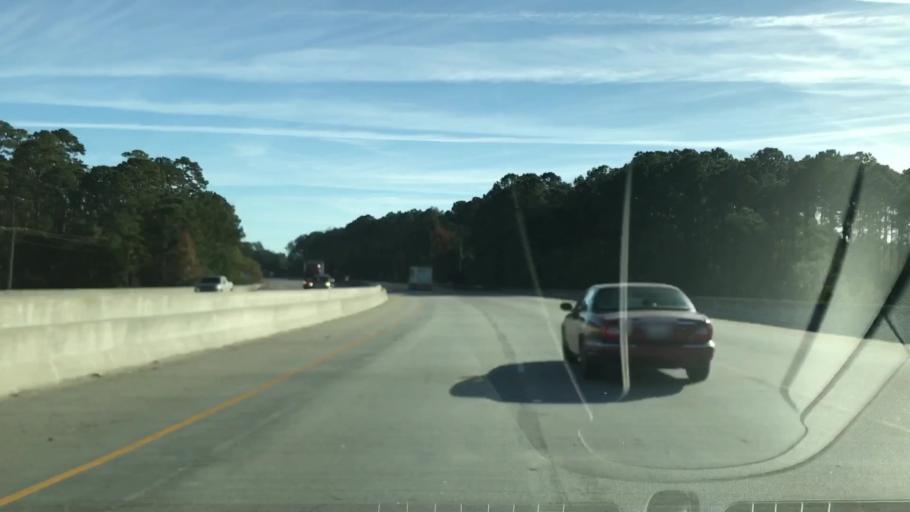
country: US
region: South Carolina
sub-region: Beaufort County
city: Bluffton
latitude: 32.2892
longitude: -80.9295
